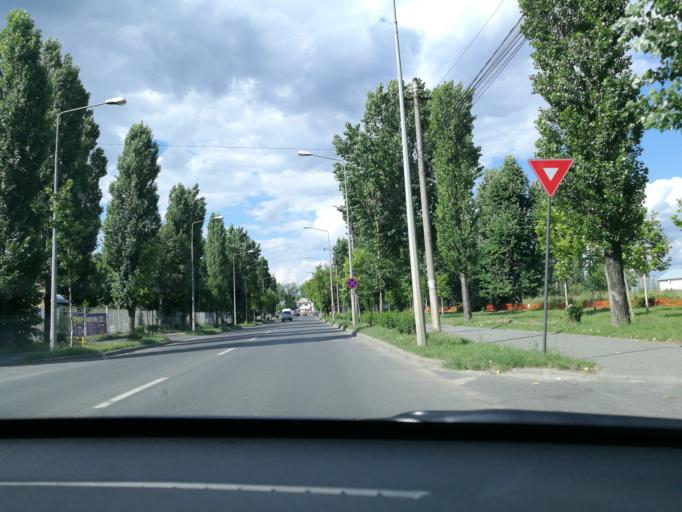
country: RO
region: Ilfov
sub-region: Comuna Glina
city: Catelu
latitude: 44.4239
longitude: 26.2200
